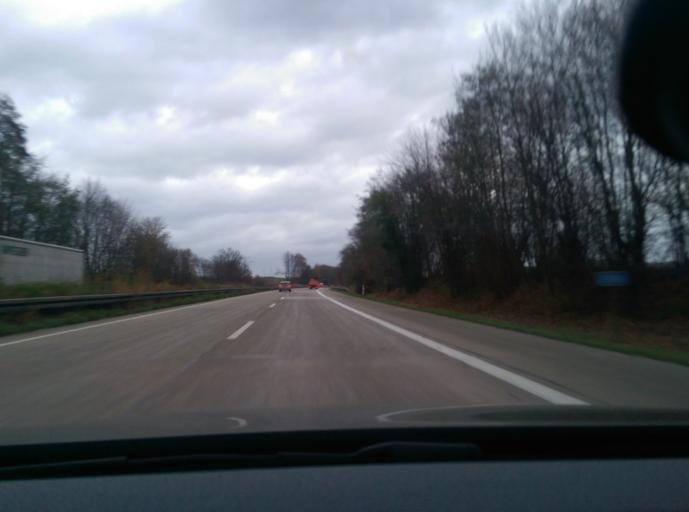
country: DE
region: Lower Saxony
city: Kalefeld
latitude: 51.8015
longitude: 10.0882
